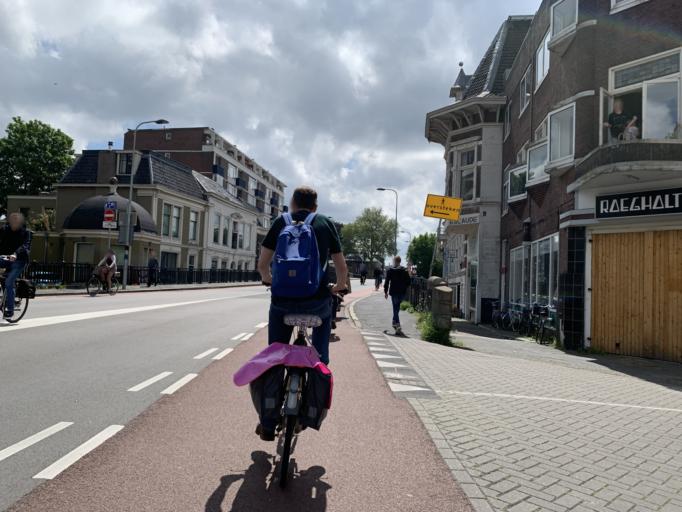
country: NL
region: Groningen
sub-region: Gemeente Groningen
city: Groningen
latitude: 53.2119
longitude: 6.5706
